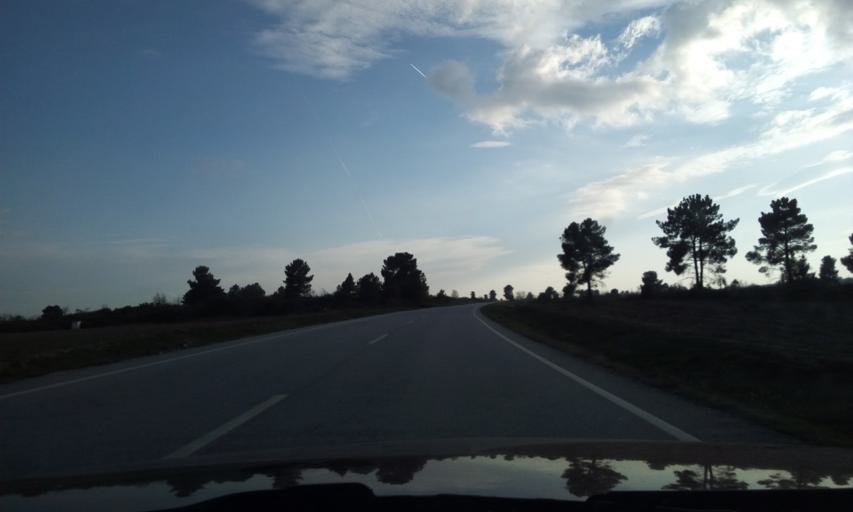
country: ES
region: Castille and Leon
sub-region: Provincia de Salamanca
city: Fuentes de Onoro
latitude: 40.6276
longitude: -6.9738
